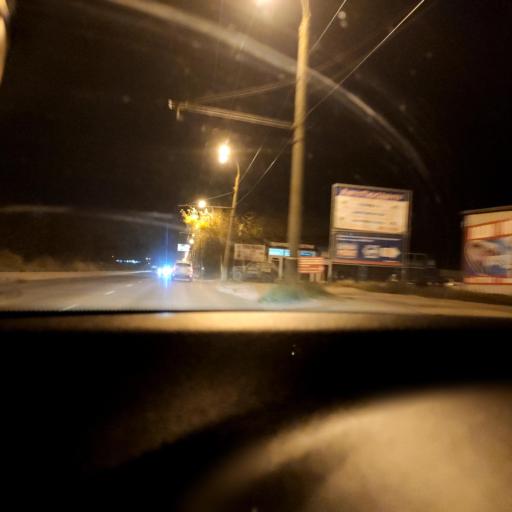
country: RU
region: Samara
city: Petra-Dubrava
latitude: 53.2525
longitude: 50.2673
